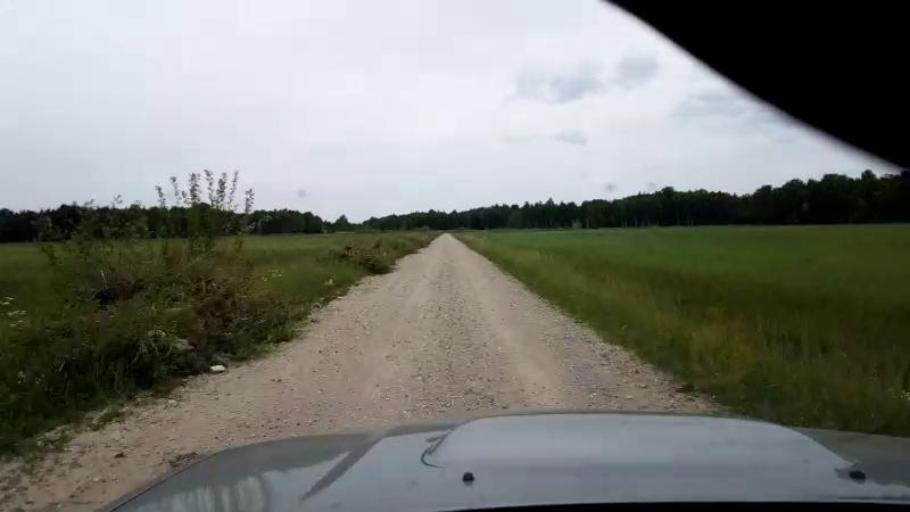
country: EE
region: Paernumaa
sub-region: Halinga vald
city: Parnu-Jaagupi
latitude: 58.5432
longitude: 24.6018
